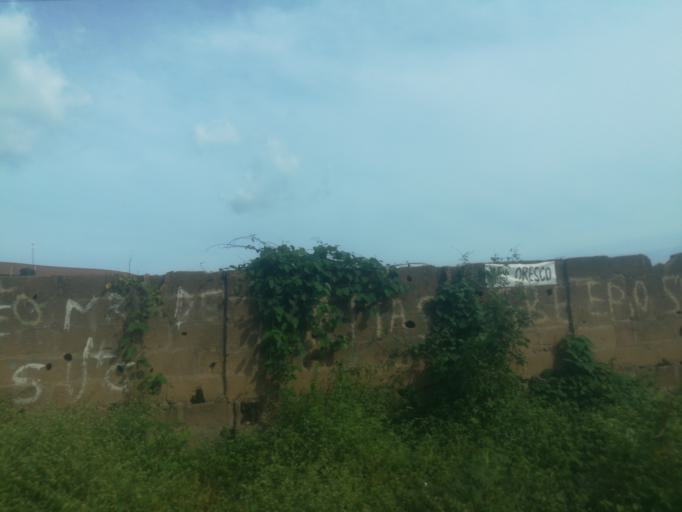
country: NG
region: Ogun
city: Abeokuta
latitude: 7.1170
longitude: 3.3290
